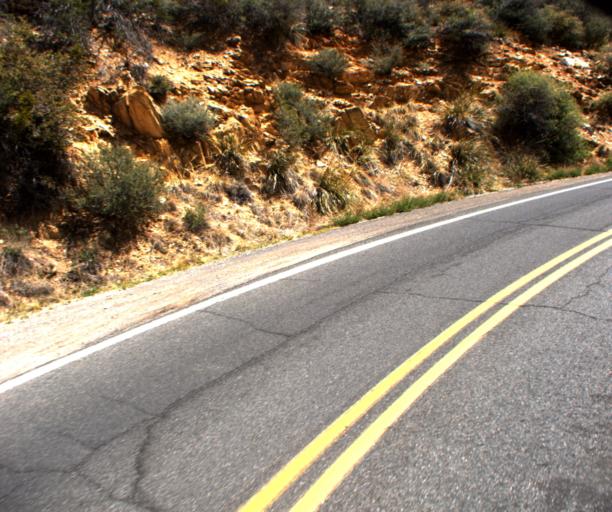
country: US
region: Arizona
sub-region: Yavapai County
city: Clarkdale
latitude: 34.7411
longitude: -112.1247
